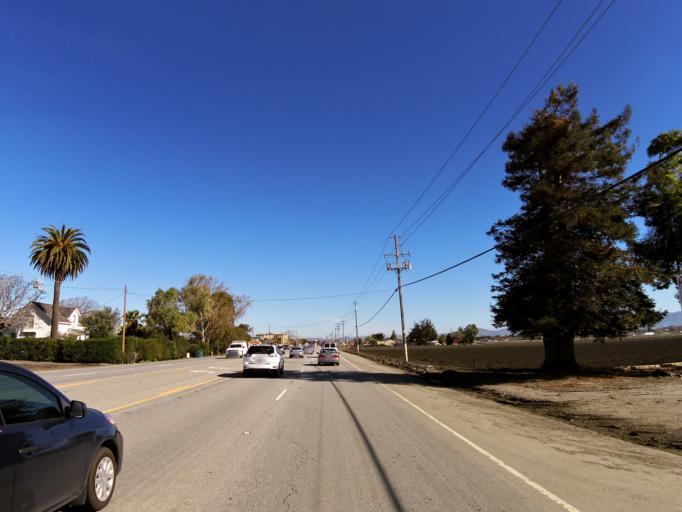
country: US
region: California
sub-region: Monterey County
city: Salinas
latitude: 36.6493
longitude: -121.6624
